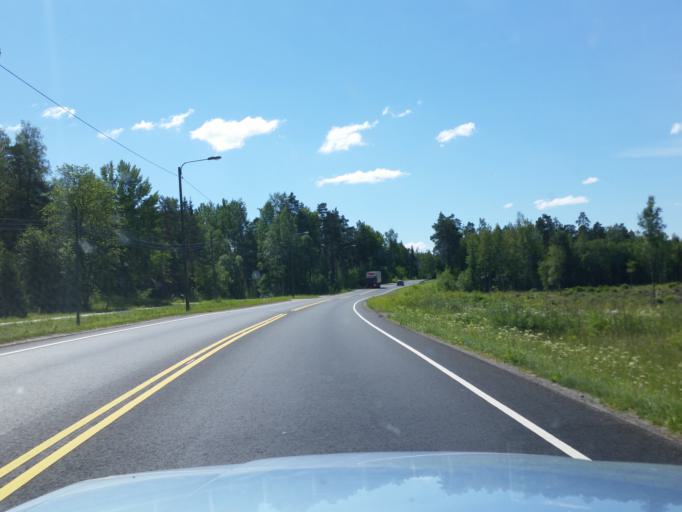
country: FI
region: Varsinais-Suomi
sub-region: Aboland-Turunmaa
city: Pargas
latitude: 60.3353
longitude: 22.3630
